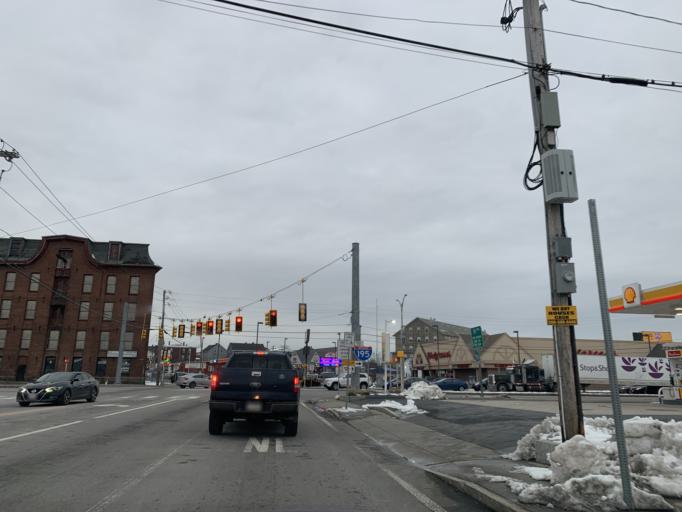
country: US
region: Massachusetts
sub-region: Bristol County
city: Fall River
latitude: 41.6951
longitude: -71.1518
